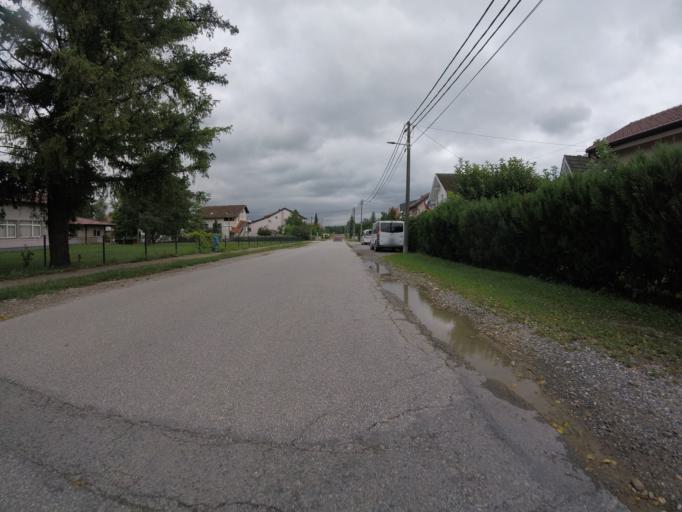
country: HR
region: Zagrebacka
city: Gradici
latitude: 45.7021
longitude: 16.0371
